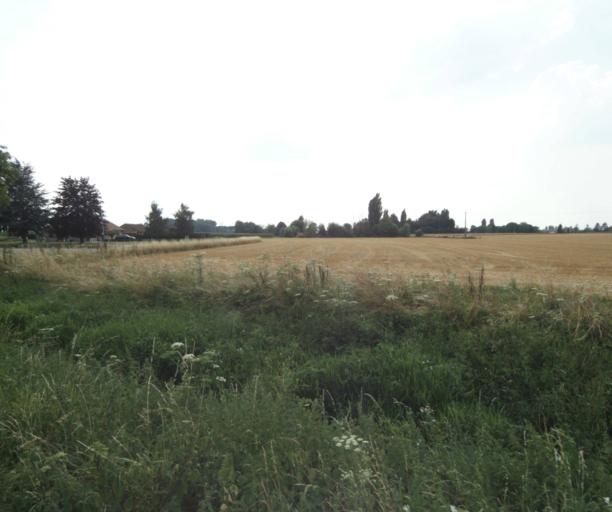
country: FR
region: Nord-Pas-de-Calais
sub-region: Departement du Nord
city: Linselles
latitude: 50.7204
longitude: 3.0677
